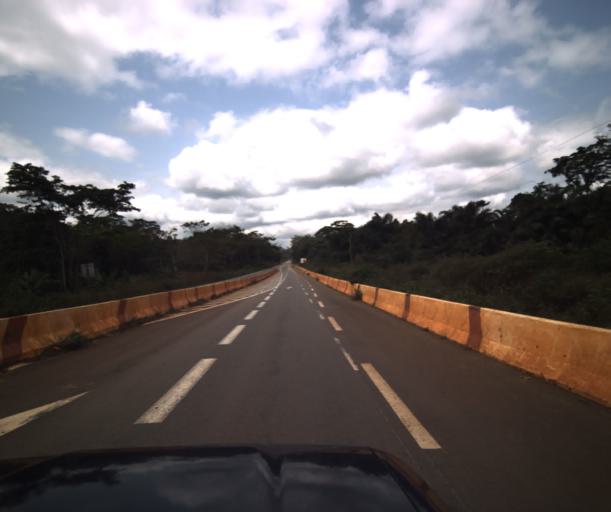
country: CM
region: Centre
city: Mbankomo
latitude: 3.7945
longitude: 11.3303
